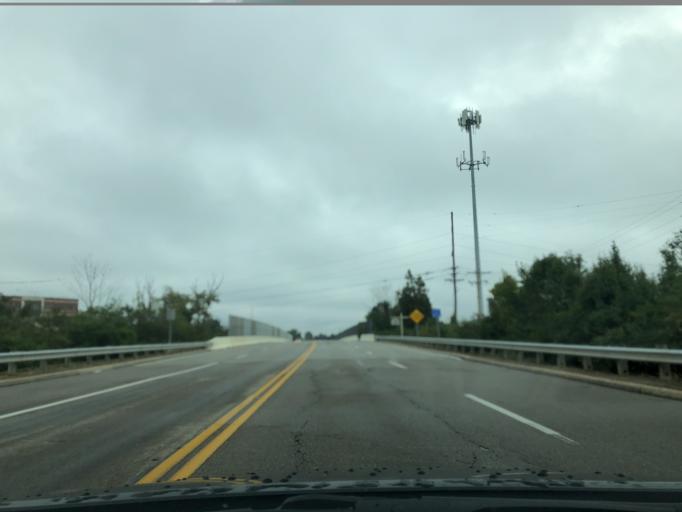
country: US
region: Ohio
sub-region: Hamilton County
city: Highpoint
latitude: 39.2824
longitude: -84.3682
